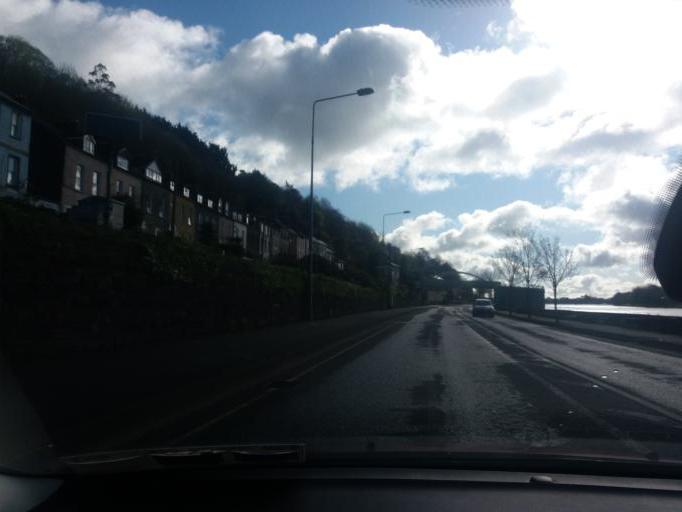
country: IE
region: Munster
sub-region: County Cork
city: Cork
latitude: 51.9030
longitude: -8.4439
